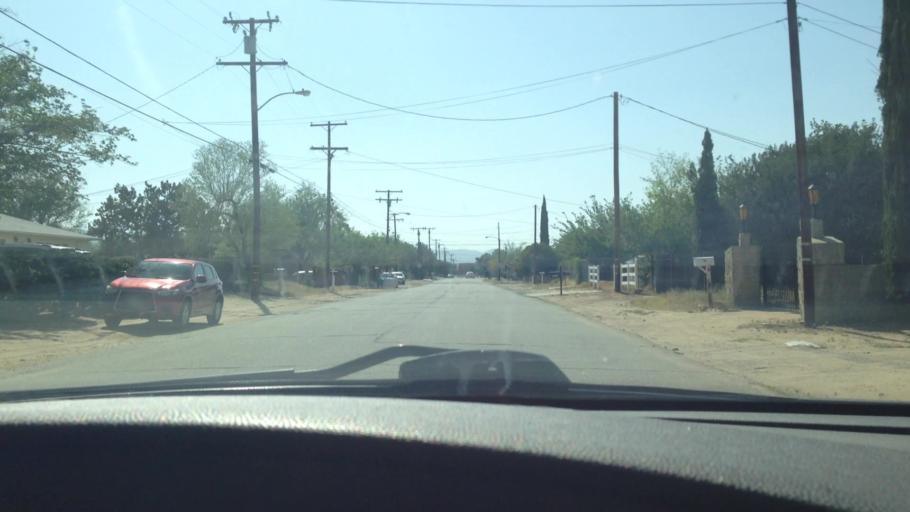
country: US
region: California
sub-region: Los Angeles County
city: Quartz Hill
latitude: 34.6584
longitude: -118.1862
